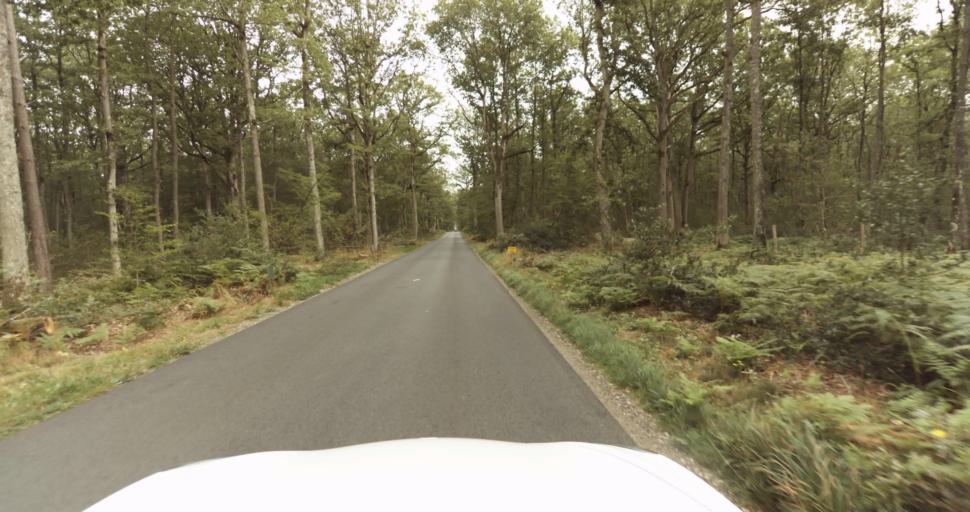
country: FR
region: Haute-Normandie
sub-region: Departement de l'Eure
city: Saint-Sebastien-de-Morsent
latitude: 48.9808
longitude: 1.0735
